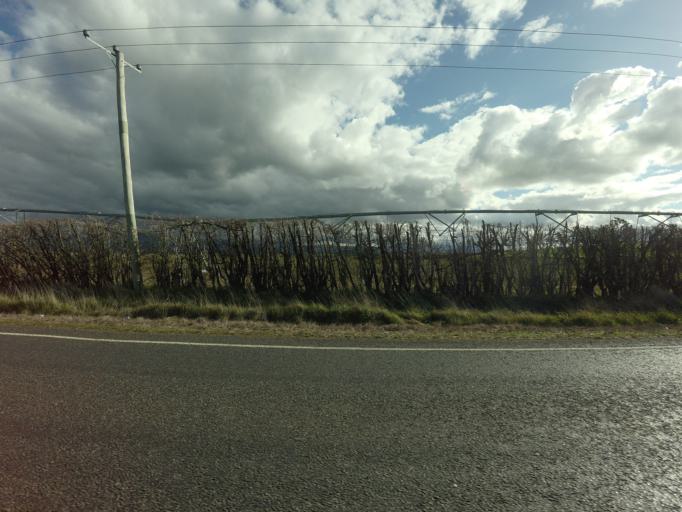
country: AU
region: Tasmania
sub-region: Northern Midlands
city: Longford
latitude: -41.7046
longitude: 147.0780
